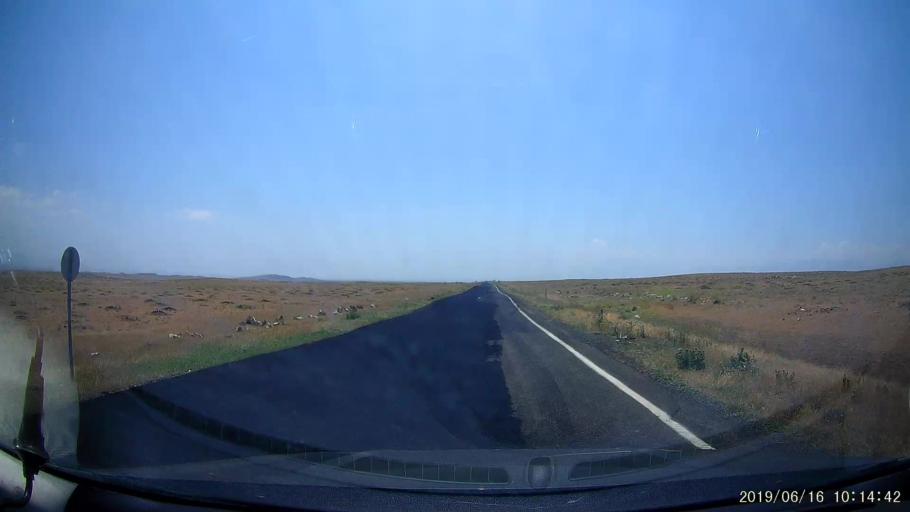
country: TR
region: Igdir
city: Tuzluca
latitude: 40.1826
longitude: 43.6681
